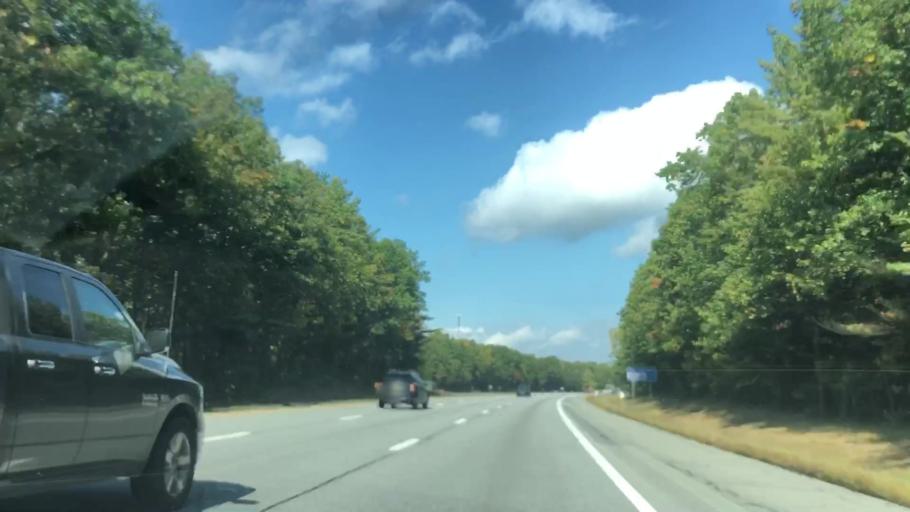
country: US
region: New York
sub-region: Warren County
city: West Glens Falls
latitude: 43.2848
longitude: -73.6805
